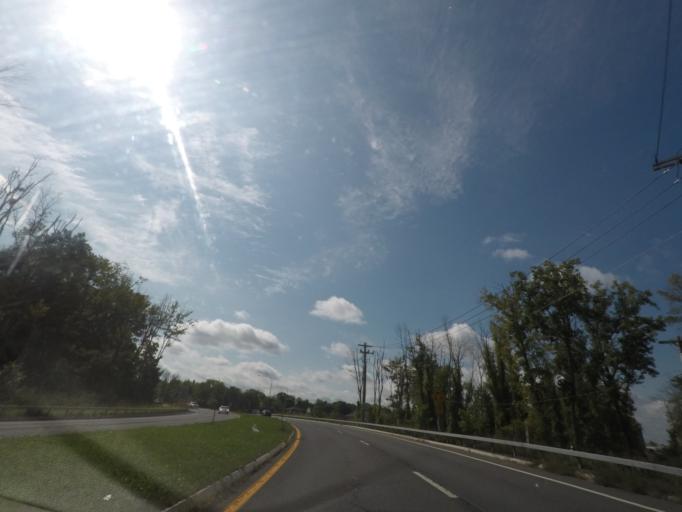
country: US
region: New York
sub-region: Albany County
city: Delmar
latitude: 42.6413
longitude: -73.8579
